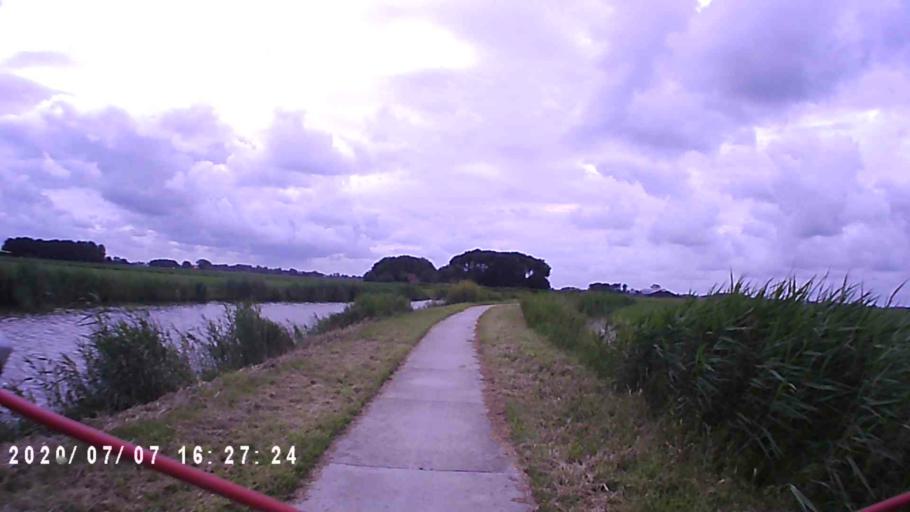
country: NL
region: Groningen
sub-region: Gemeente Winsum
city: Winsum
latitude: 53.3580
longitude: 6.5594
